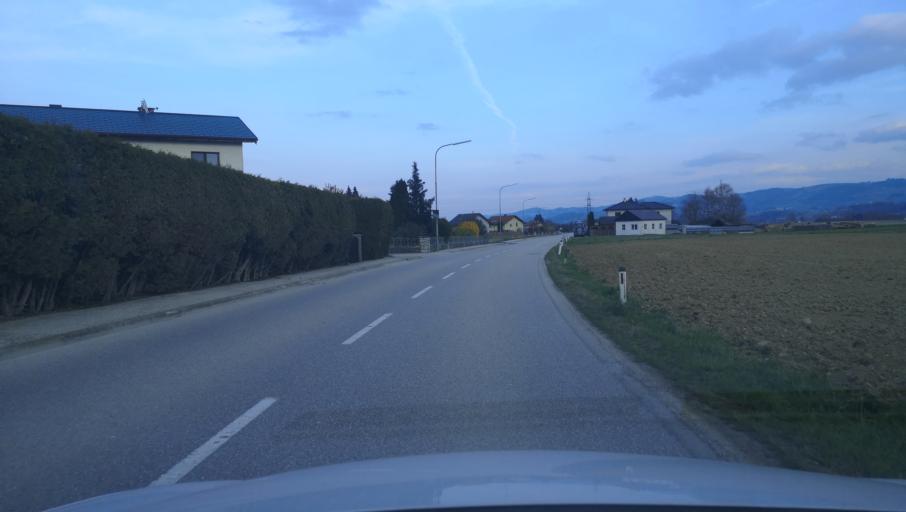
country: AT
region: Lower Austria
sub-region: Politischer Bezirk Amstetten
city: Winklarn
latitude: 48.0766
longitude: 14.8305
